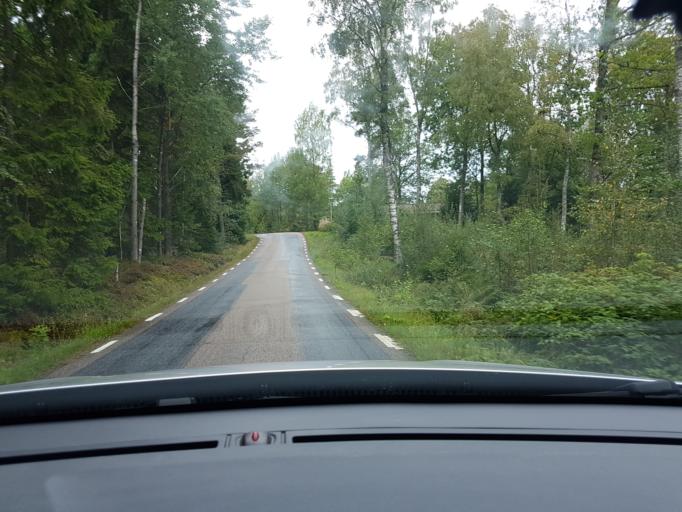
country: SE
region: Vaestra Goetaland
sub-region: Ale Kommun
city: Alvangen
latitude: 57.9014
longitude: 12.1832
